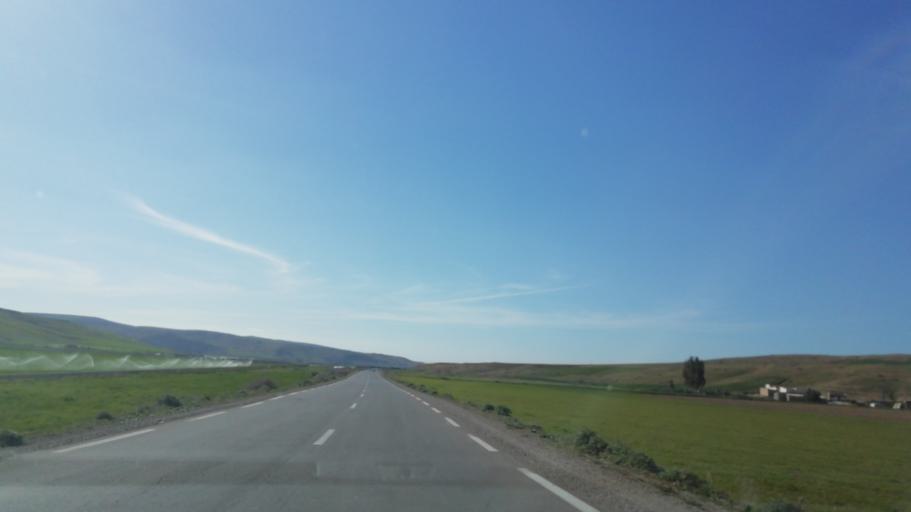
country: DZ
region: Mascara
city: Oued el Abtal
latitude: 35.4498
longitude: 0.8029
